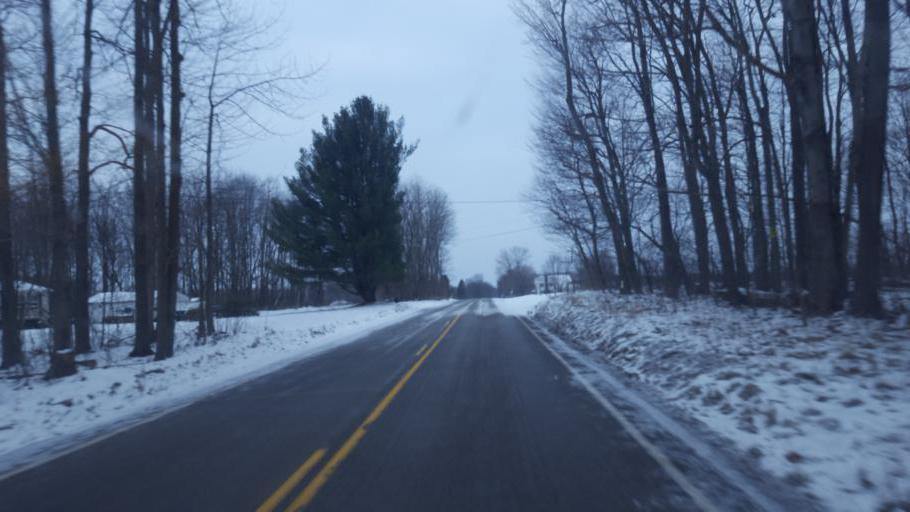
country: US
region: Pennsylvania
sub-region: Mercer County
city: Stoneboro
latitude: 41.4083
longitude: -80.0549
